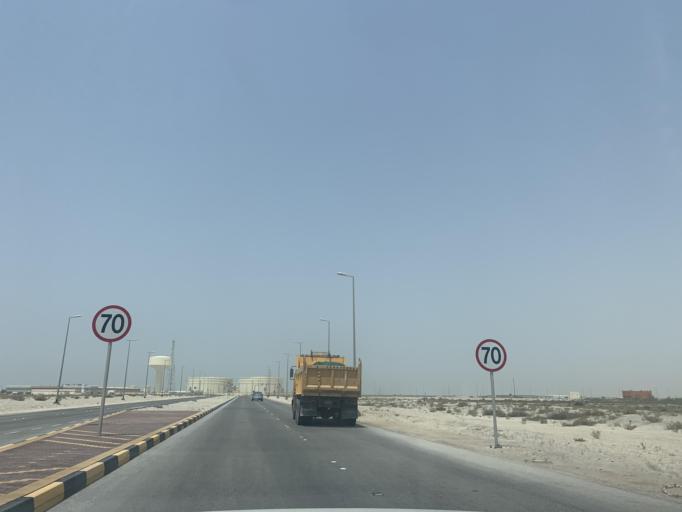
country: BH
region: Central Governorate
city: Dar Kulayb
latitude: 25.8388
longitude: 50.5915
